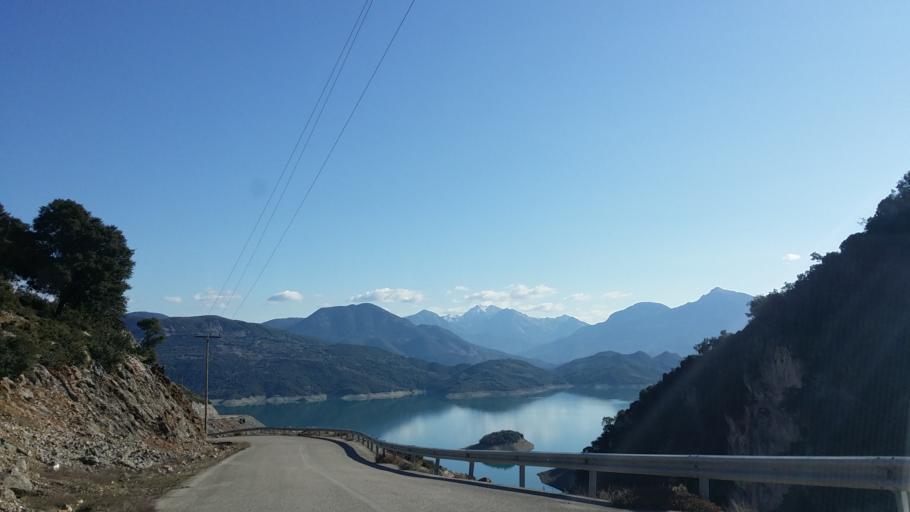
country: GR
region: Central Greece
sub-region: Nomos Evrytanias
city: Kerasochori
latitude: 38.9655
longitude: 21.4692
